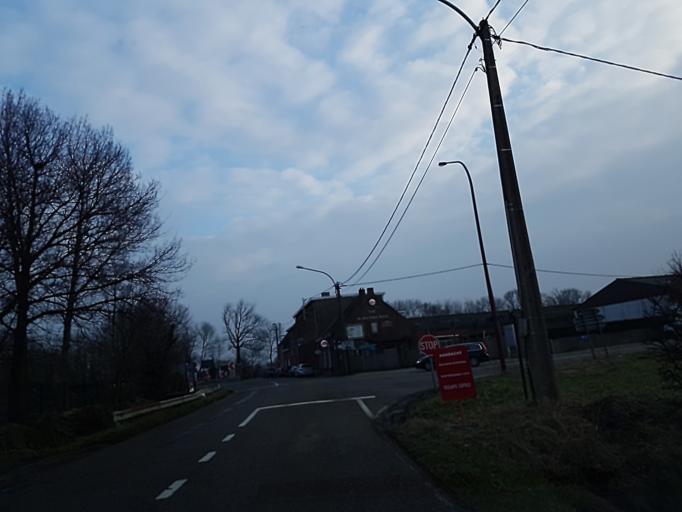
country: BE
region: Flanders
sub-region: Provincie Antwerpen
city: Stabroek
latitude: 51.3033
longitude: 4.3932
